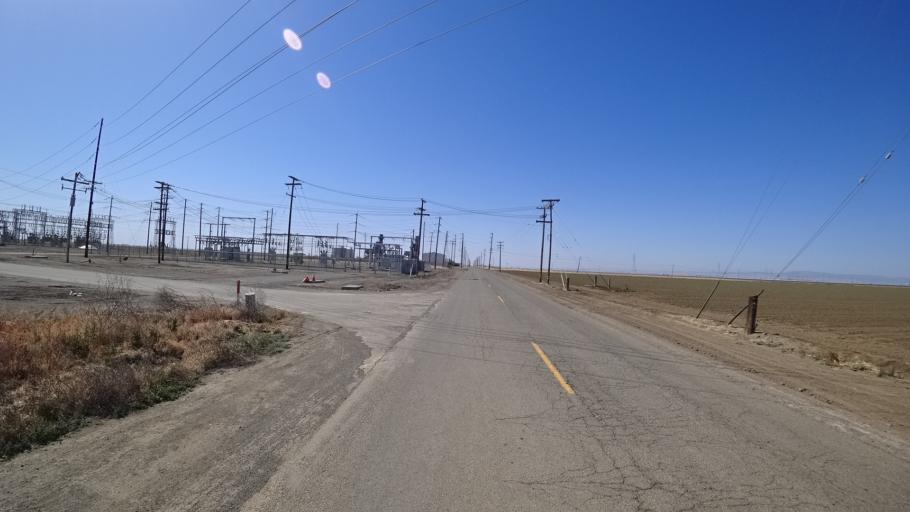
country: US
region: California
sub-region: Kings County
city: Lemoore Station
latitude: 36.2428
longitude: -119.9052
